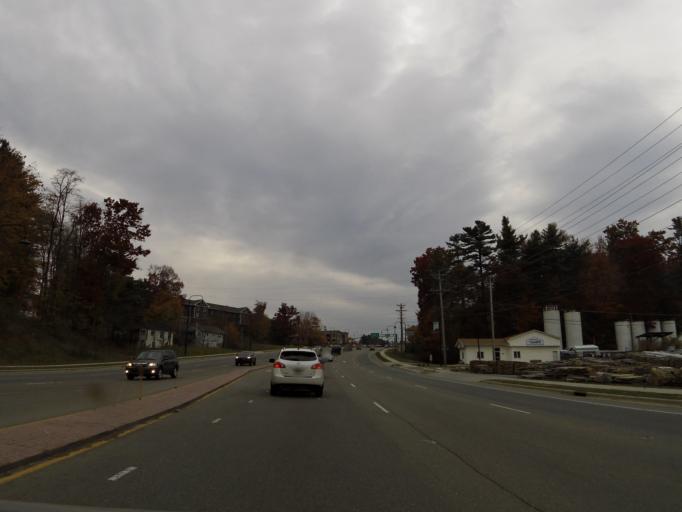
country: US
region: North Carolina
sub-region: Watauga County
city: Boone
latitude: 36.2172
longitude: -81.6652
